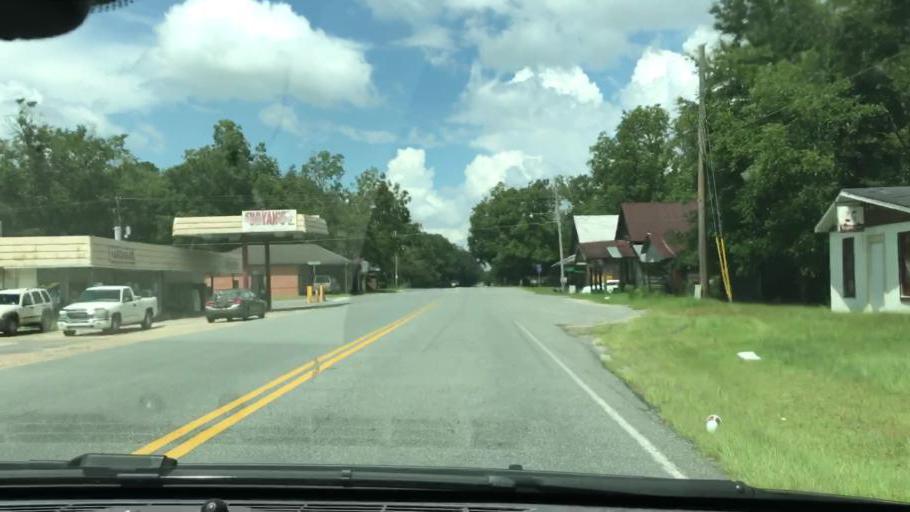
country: US
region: Florida
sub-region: Jackson County
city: Malone
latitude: 30.9261
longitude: -85.1186
